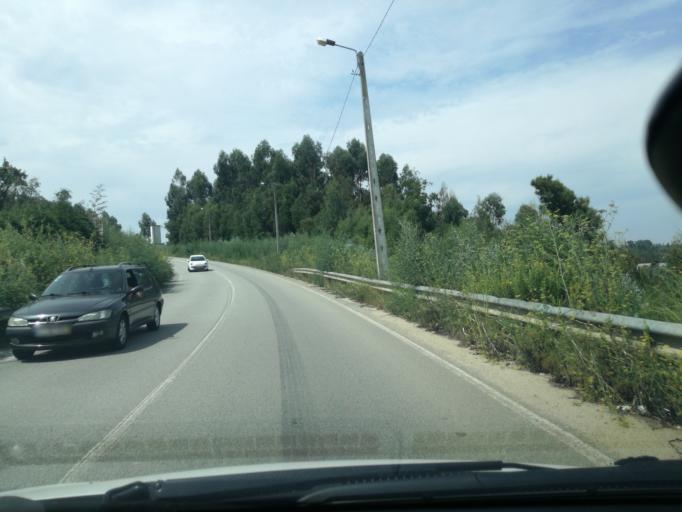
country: PT
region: Aveiro
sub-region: Santa Maria da Feira
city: Nogueira da Regedoura
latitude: 41.0141
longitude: -8.5878
